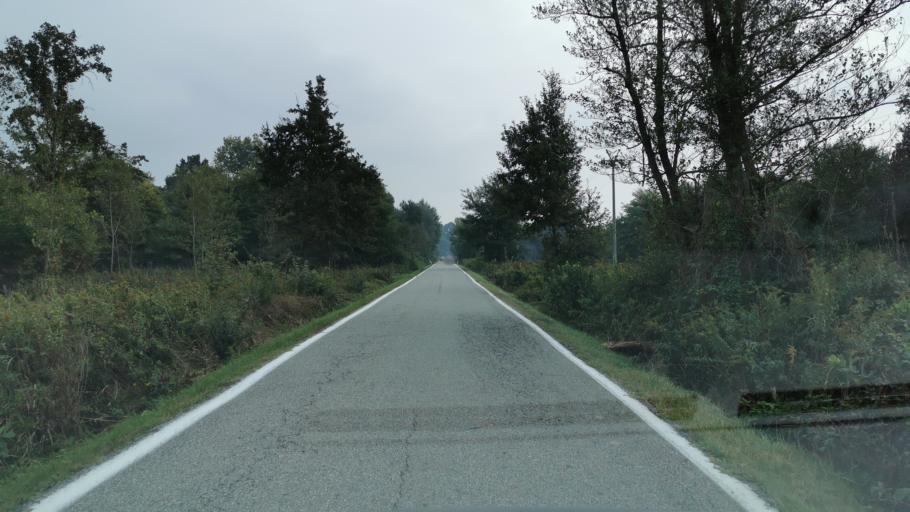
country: IT
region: Piedmont
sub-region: Provincia di Torino
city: Foglizzo
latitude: 45.2487
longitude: 7.8319
